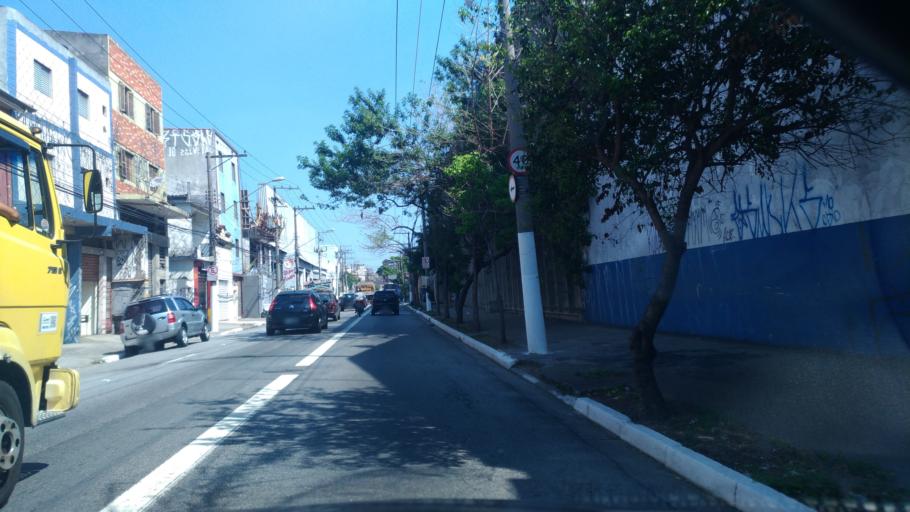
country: BR
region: Sao Paulo
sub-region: Sao Paulo
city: Sao Paulo
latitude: -23.5328
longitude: -46.6027
